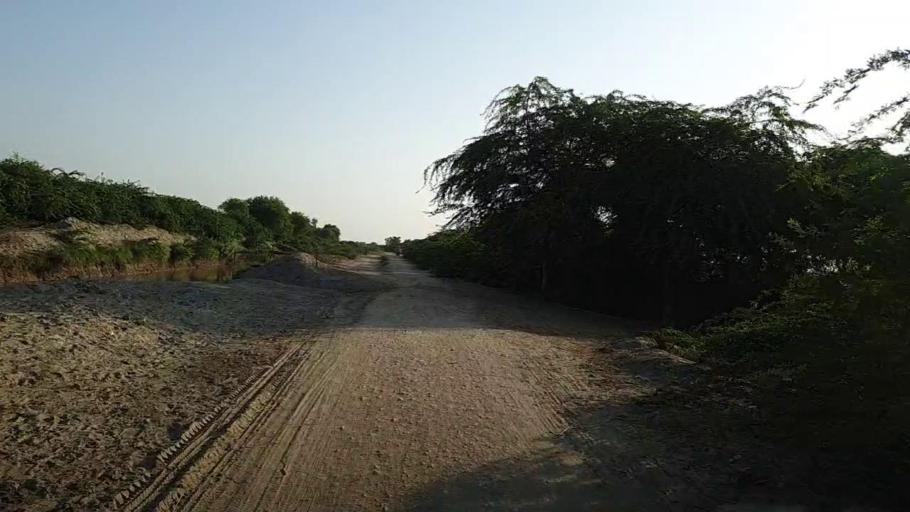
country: PK
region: Sindh
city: Kario
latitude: 24.7278
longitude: 68.6687
